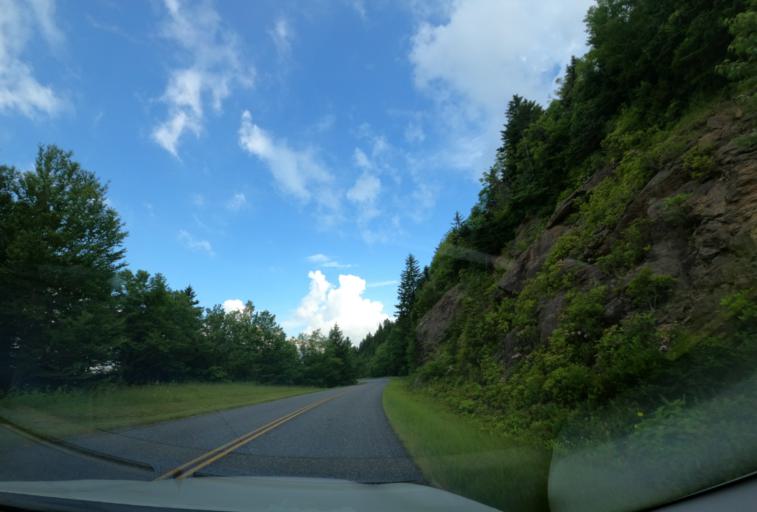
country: US
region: North Carolina
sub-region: Haywood County
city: Hazelwood
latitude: 35.3736
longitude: -83.0028
